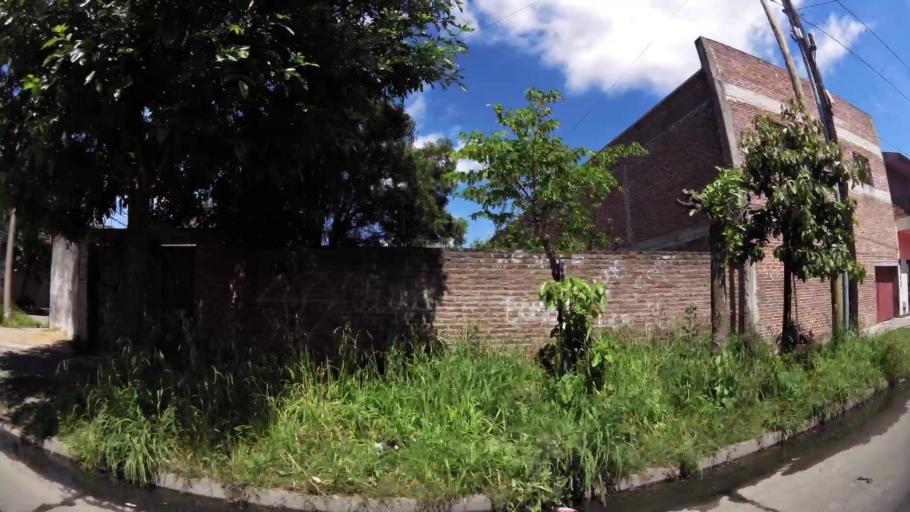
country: AR
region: Buenos Aires F.D.
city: Villa Lugano
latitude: -34.6874
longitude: -58.4339
